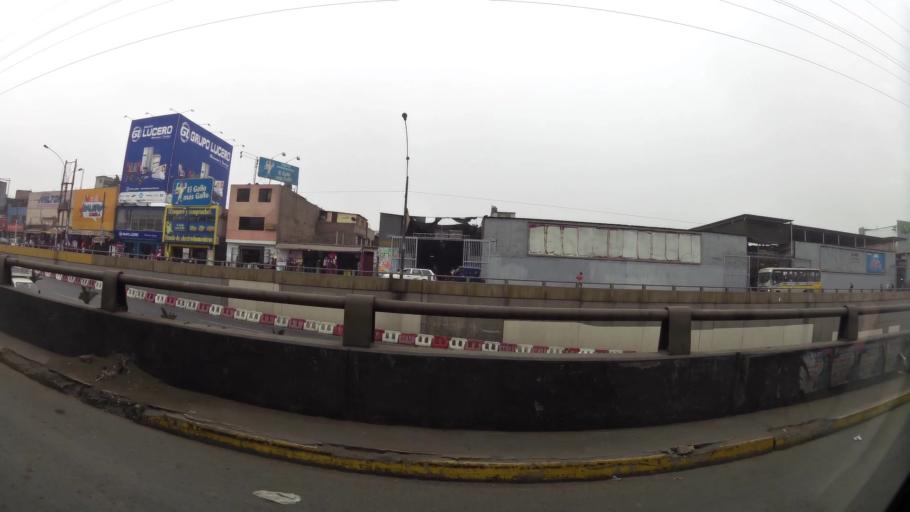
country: PE
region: Lima
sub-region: Lima
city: Carabayllo
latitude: -11.8638
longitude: -77.0757
